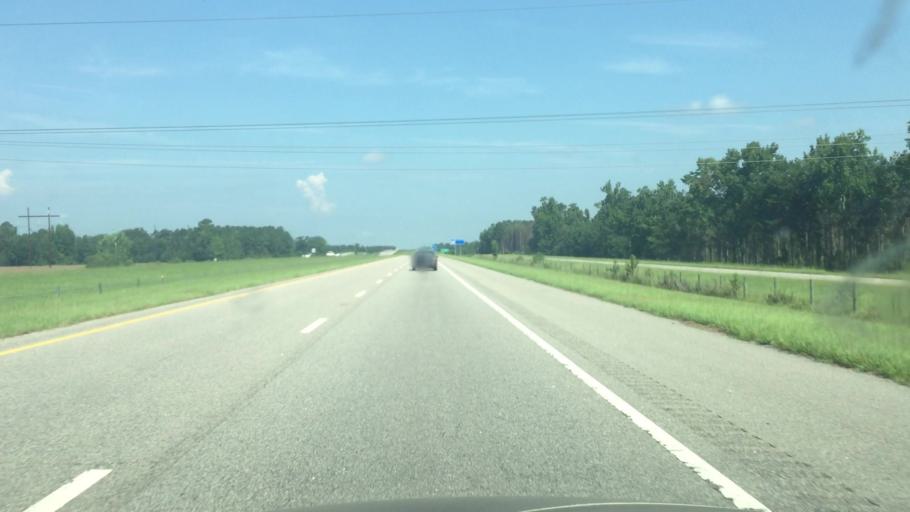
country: US
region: North Carolina
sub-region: Robeson County
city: Pembroke
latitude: 34.6421
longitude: -79.2364
